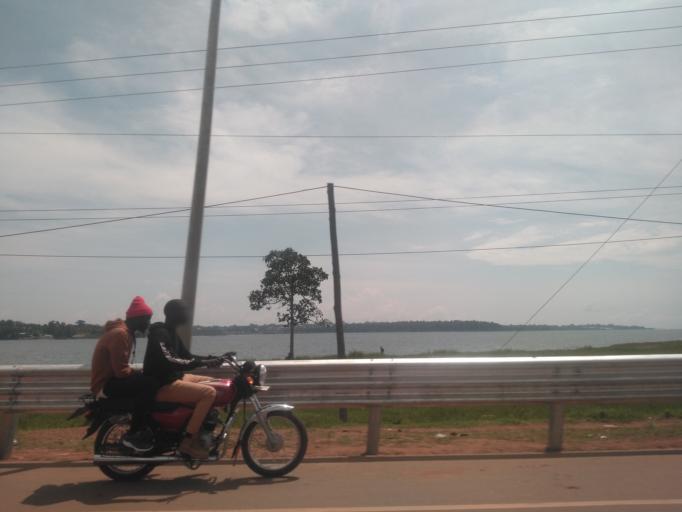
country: UG
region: Central Region
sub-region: Wakiso District
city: Entebbe
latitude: 0.0856
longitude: 32.4839
